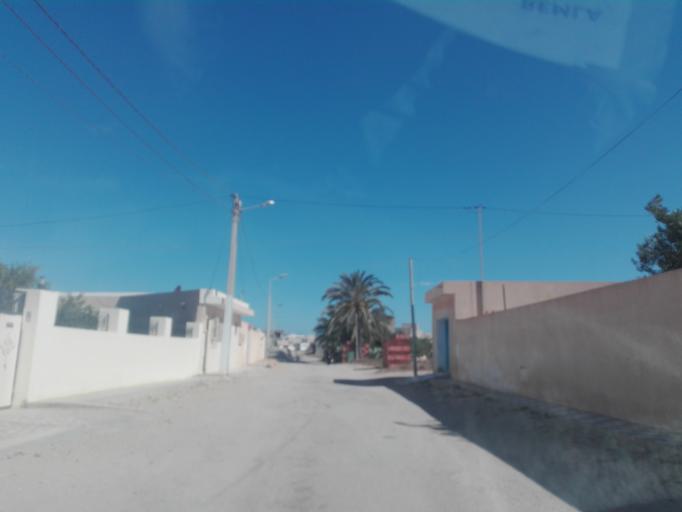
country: TN
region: Safaqis
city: Al Qarmadah
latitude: 34.7083
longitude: 11.1996
